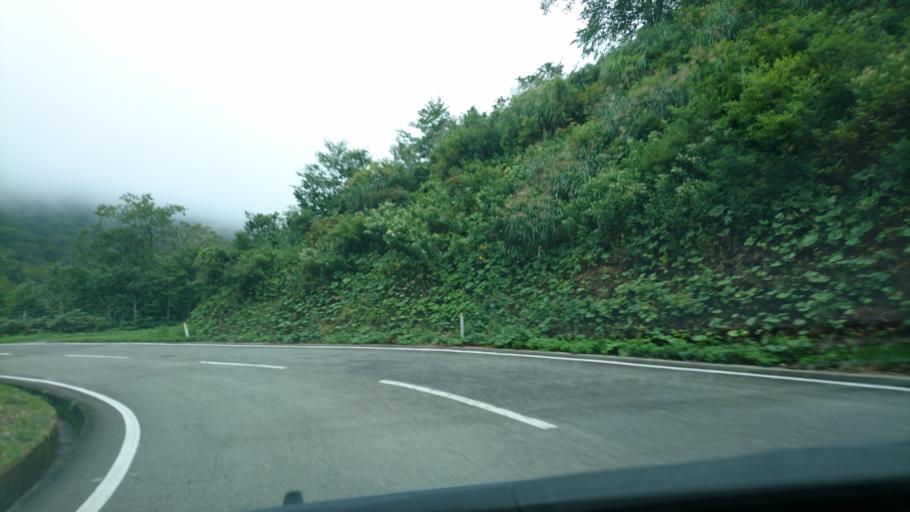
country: JP
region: Akita
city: Yuzawa
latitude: 38.9757
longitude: 140.7534
